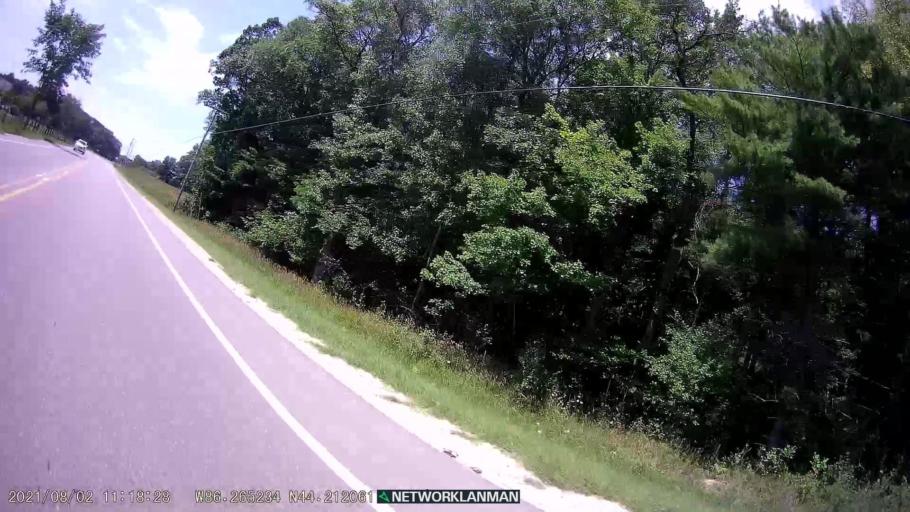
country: US
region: Michigan
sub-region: Manistee County
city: Manistee
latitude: 44.2121
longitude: -86.2652
